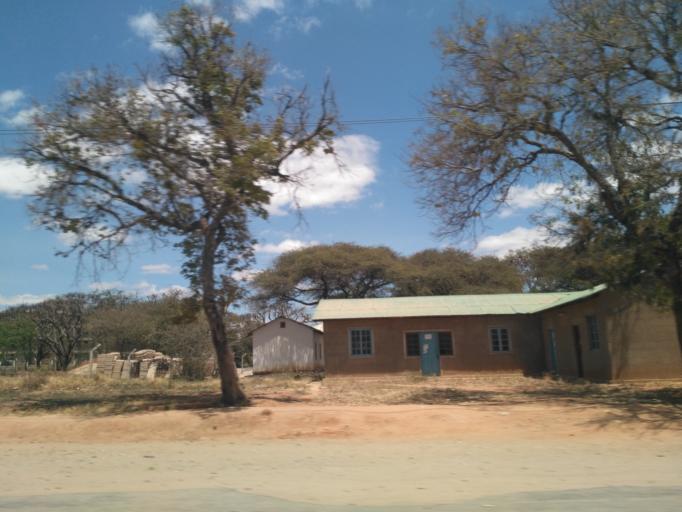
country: TZ
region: Dodoma
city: Dodoma
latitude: -6.1848
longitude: 35.7460
